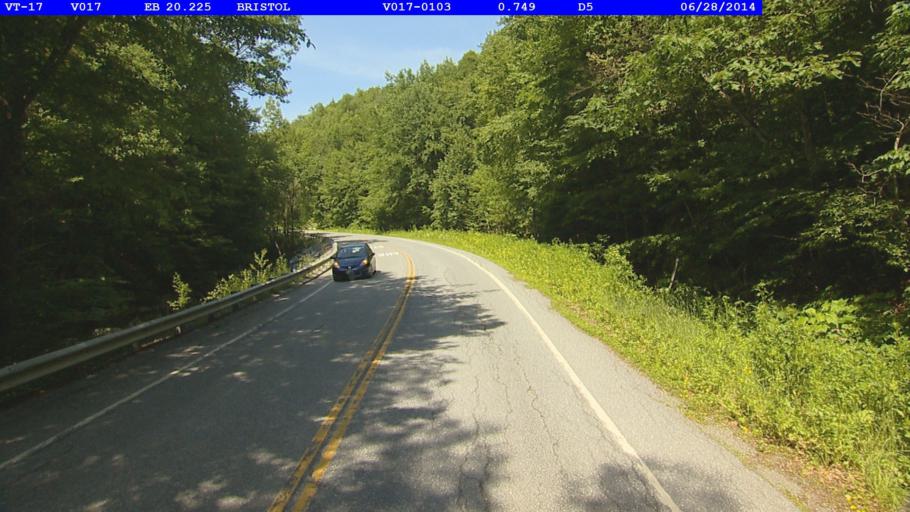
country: US
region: Vermont
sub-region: Addison County
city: Bristol
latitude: 44.1546
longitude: -73.0432
